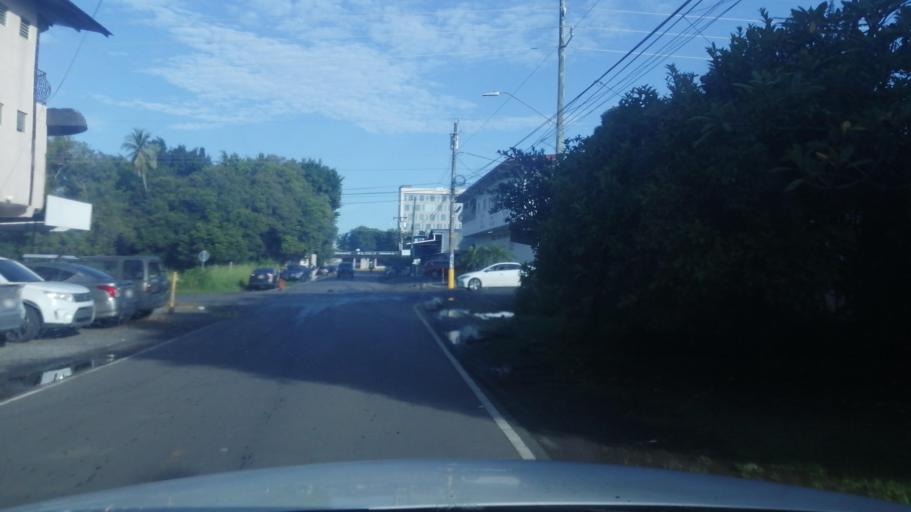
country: PA
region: Chiriqui
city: David
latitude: 8.4256
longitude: -82.4361
